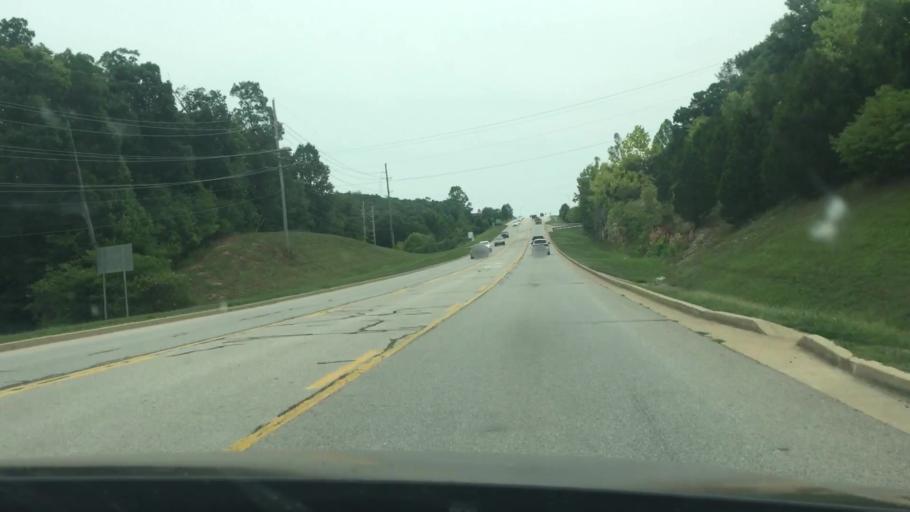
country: US
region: Missouri
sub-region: Miller County
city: Lake Ozark
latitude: 38.1916
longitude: -92.6526
